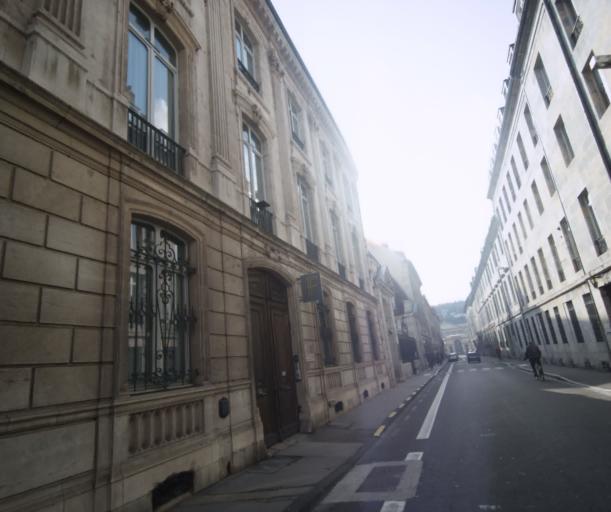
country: FR
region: Franche-Comte
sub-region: Departement du Doubs
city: Besancon
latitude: 47.2345
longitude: 6.0241
